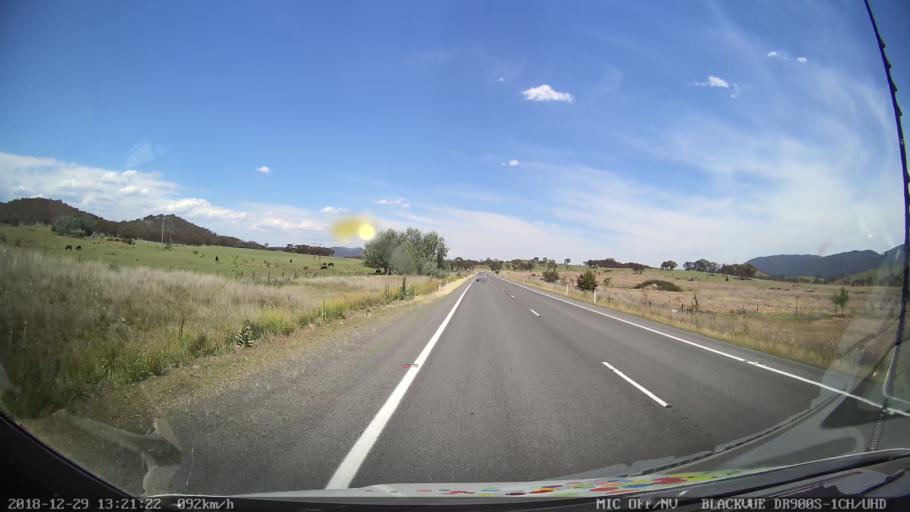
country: AU
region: Australian Capital Territory
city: Macarthur
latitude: -35.7914
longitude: 149.1638
